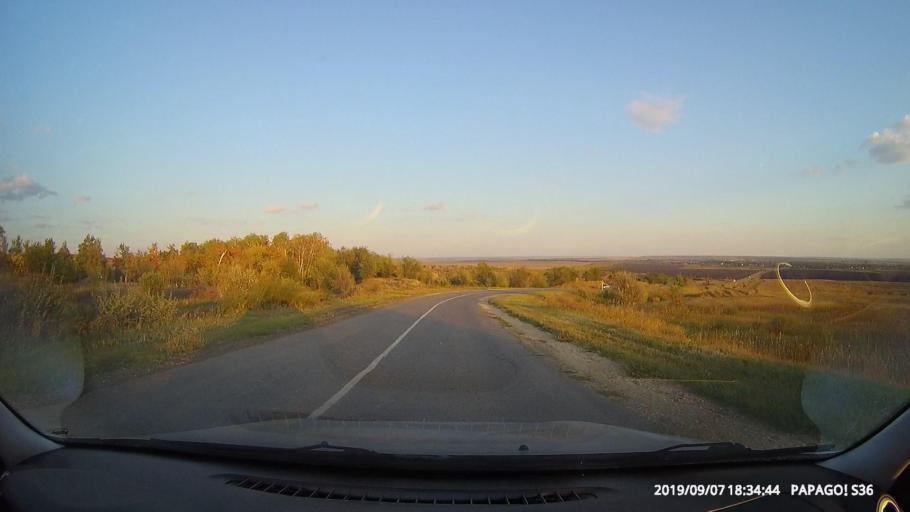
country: RU
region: Samara
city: Chapayevsk
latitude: 52.9924
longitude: 49.7759
